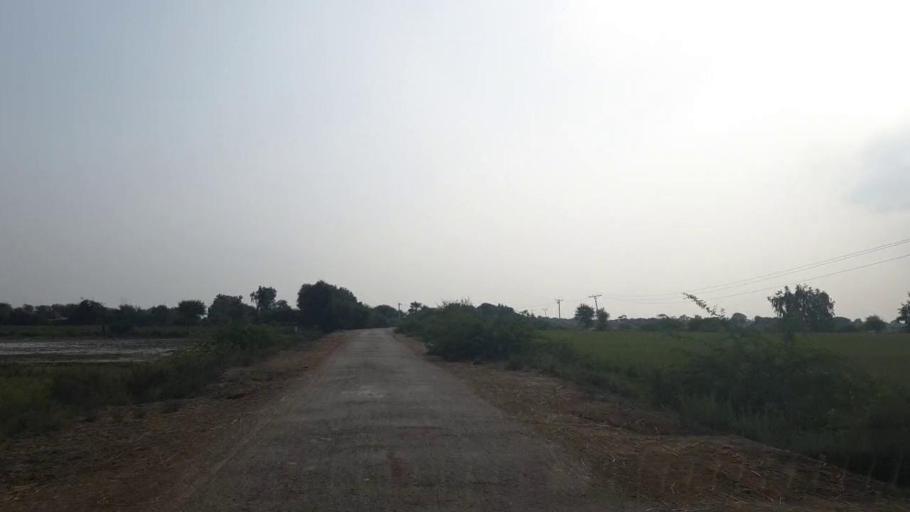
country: PK
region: Sindh
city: Badin
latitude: 24.6403
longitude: 68.6938
